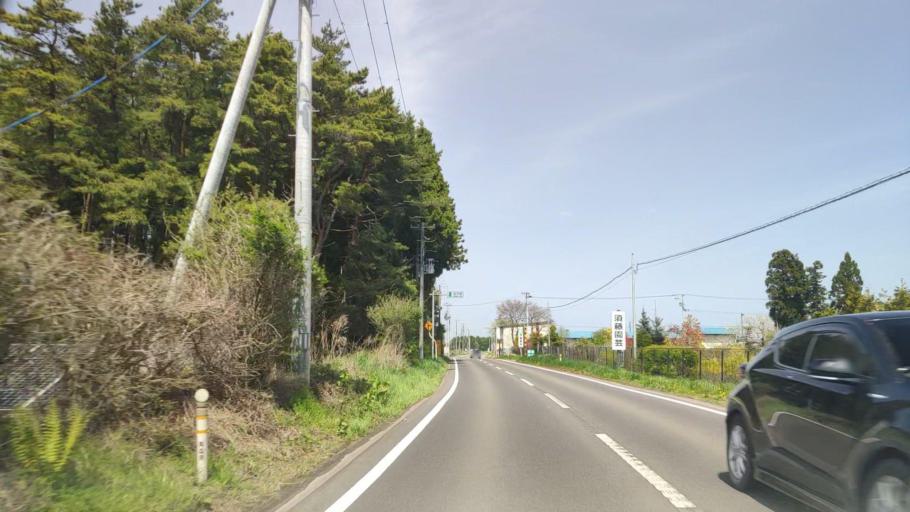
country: JP
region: Aomori
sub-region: Hachinohe Shi
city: Uchimaru
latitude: 40.5362
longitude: 141.4021
